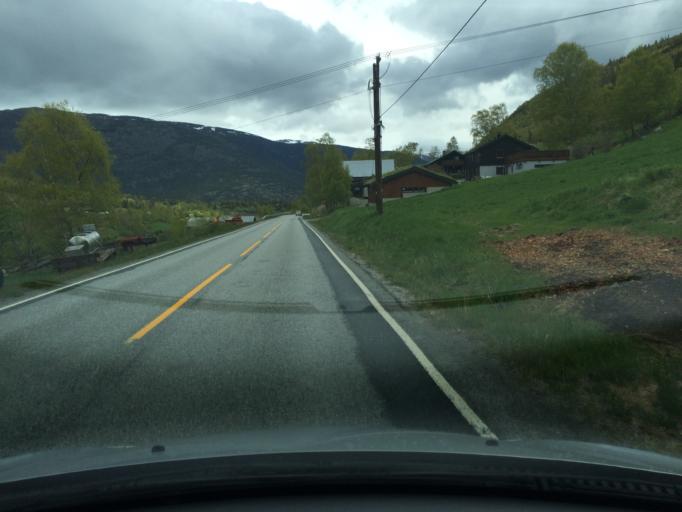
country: NO
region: Oppland
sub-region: Lom
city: Fossbergom
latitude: 61.8253
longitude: 8.5434
